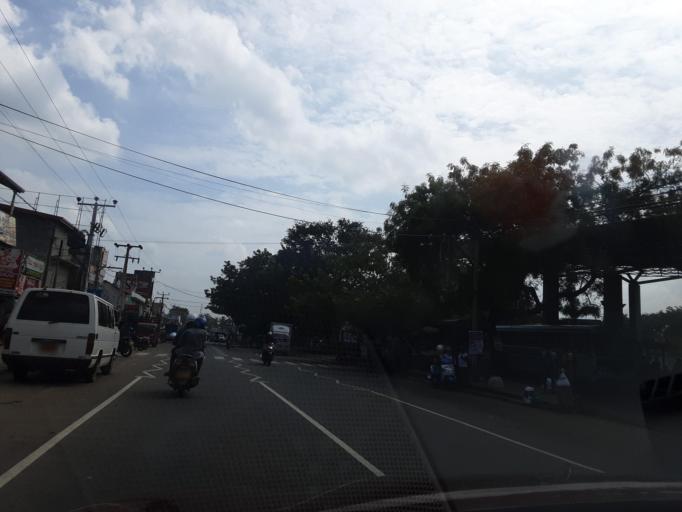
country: LK
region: Northern Province
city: Vavuniya
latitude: 8.5395
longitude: 80.4928
